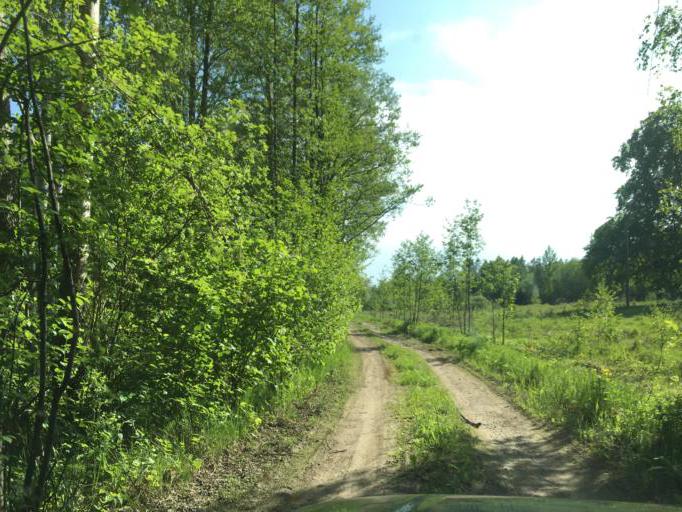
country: LV
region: Dundaga
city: Dundaga
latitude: 57.6030
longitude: 22.5083
